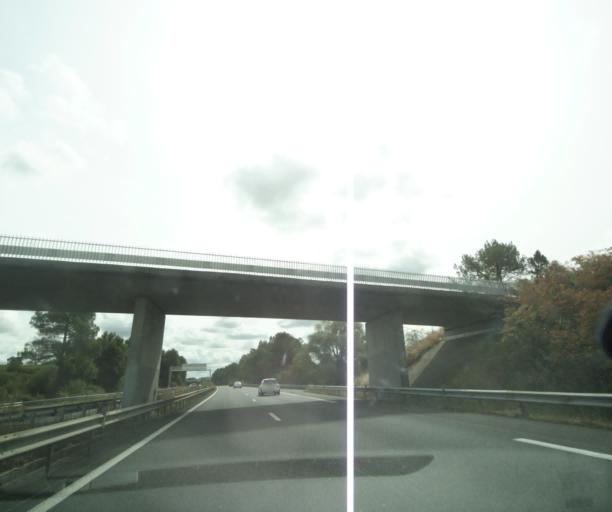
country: FR
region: Aquitaine
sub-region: Departement de la Gironde
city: Reignac
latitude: 45.2294
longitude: -0.5229
